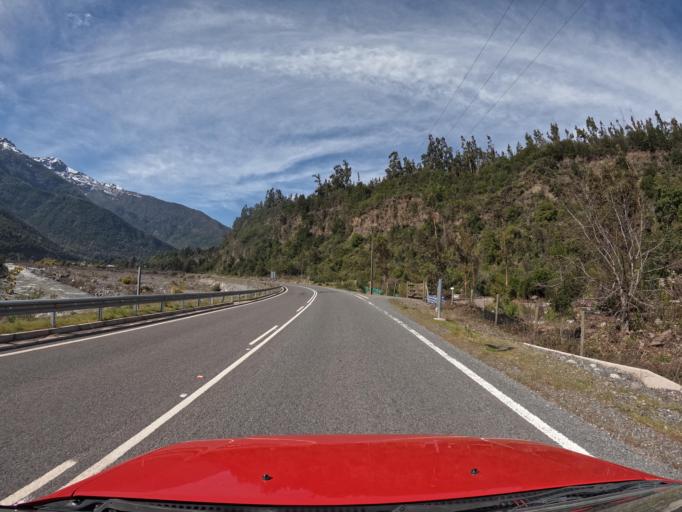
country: CL
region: Maule
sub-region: Provincia de Curico
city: Teno
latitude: -35.0038
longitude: -70.8281
